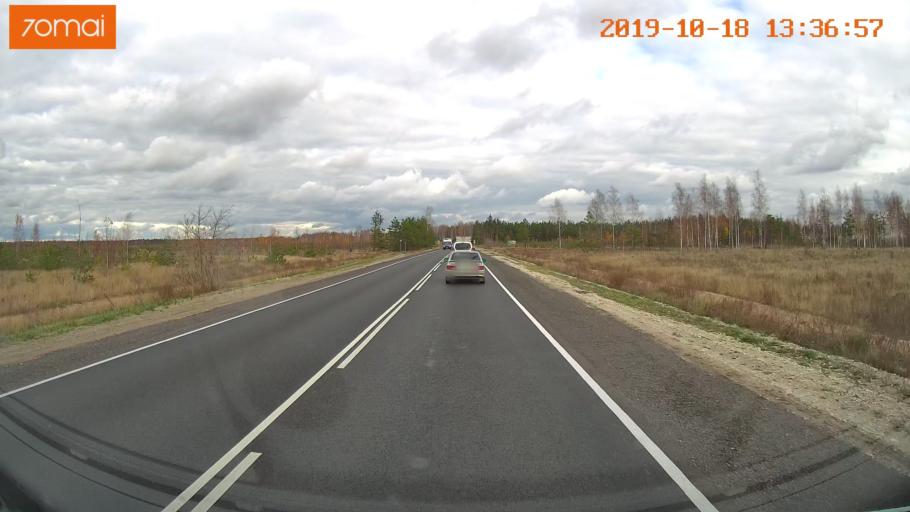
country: RU
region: Rjazan
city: Solotcha
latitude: 54.8754
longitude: 39.9895
